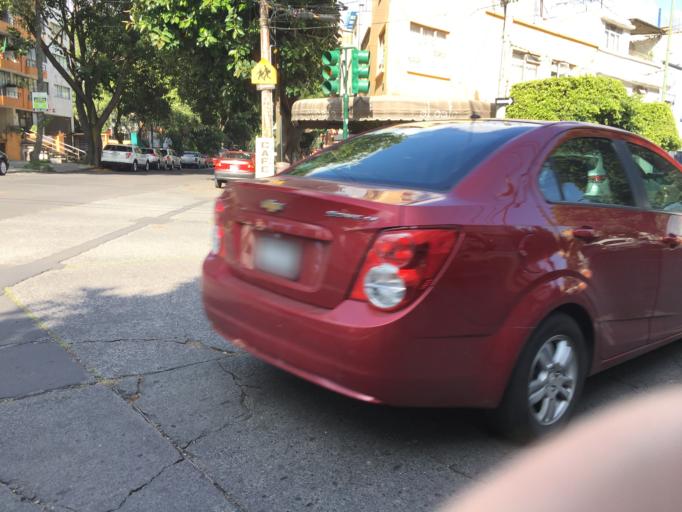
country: MX
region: Mexico City
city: Colonia del Valle
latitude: 19.3734
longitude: -99.1528
